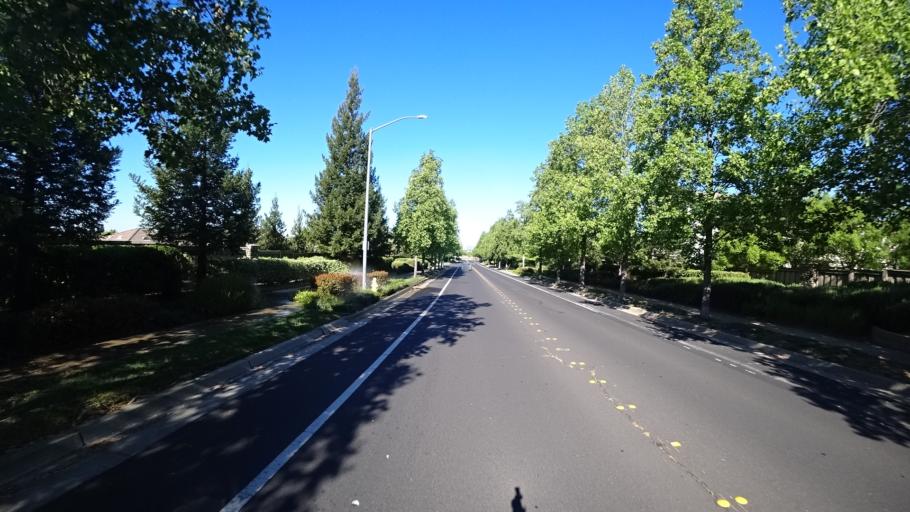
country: US
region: California
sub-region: Placer County
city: Rocklin
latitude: 38.7897
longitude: -121.2708
